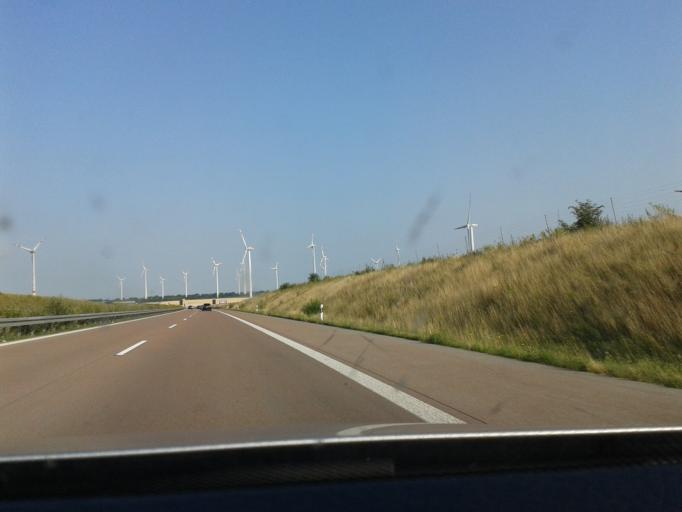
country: DE
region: Saxony-Anhalt
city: Obhausen
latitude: 51.4070
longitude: 11.6902
